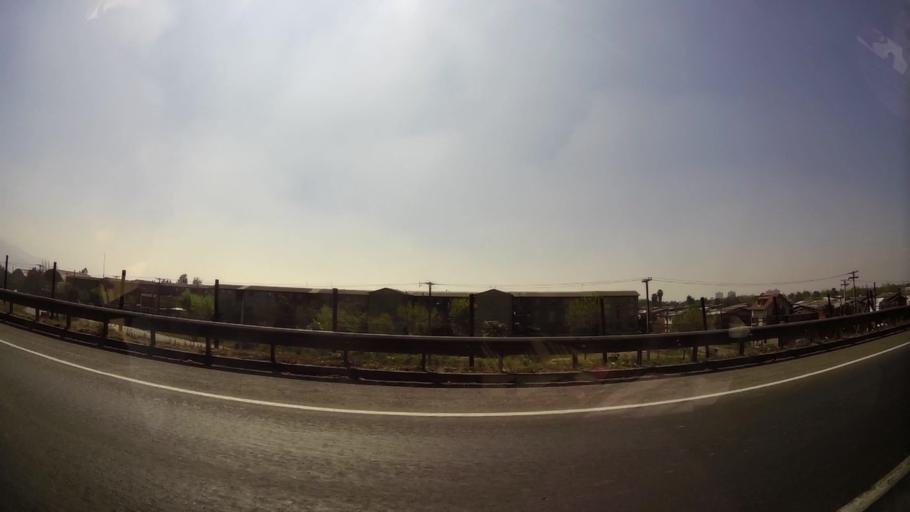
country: CL
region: Santiago Metropolitan
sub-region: Provincia de Santiago
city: Lo Prado
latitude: -33.4928
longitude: -70.7646
